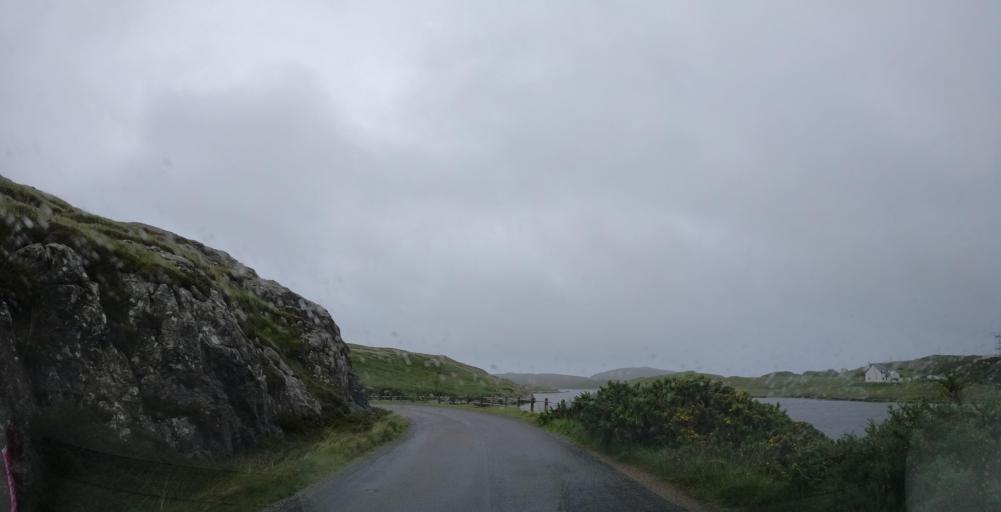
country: GB
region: Scotland
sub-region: Eilean Siar
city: Barra
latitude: 56.9919
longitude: -7.4201
